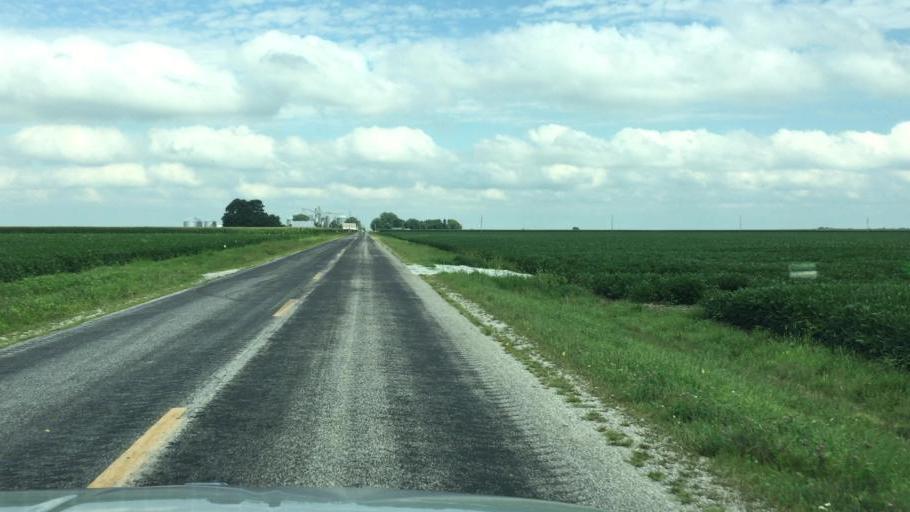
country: US
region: Illinois
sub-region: Hancock County
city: Carthage
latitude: 40.5207
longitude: -91.1848
